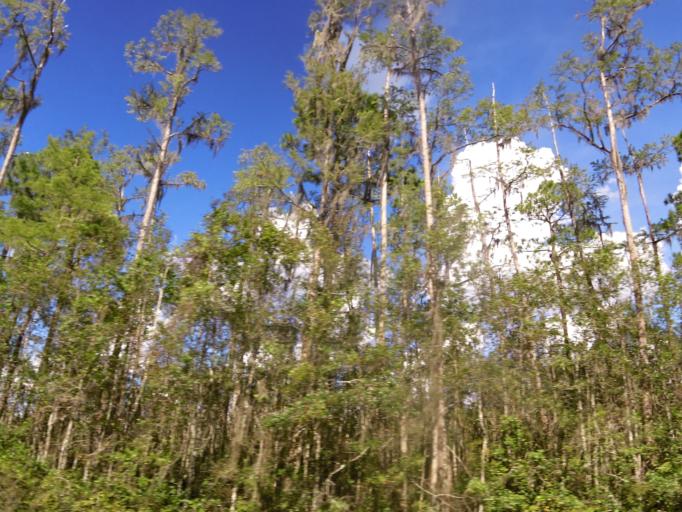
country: US
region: Georgia
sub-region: Echols County
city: Statenville
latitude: 30.7388
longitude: -83.0949
